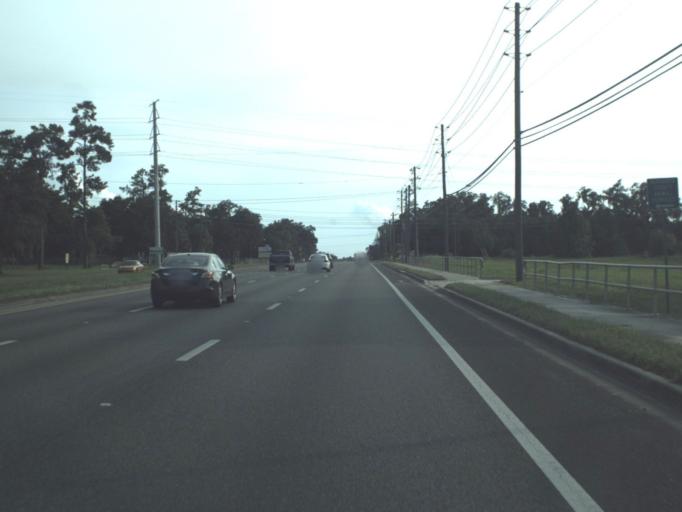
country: US
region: Florida
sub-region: Hernando County
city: South Brooksville
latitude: 28.5281
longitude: -82.4107
